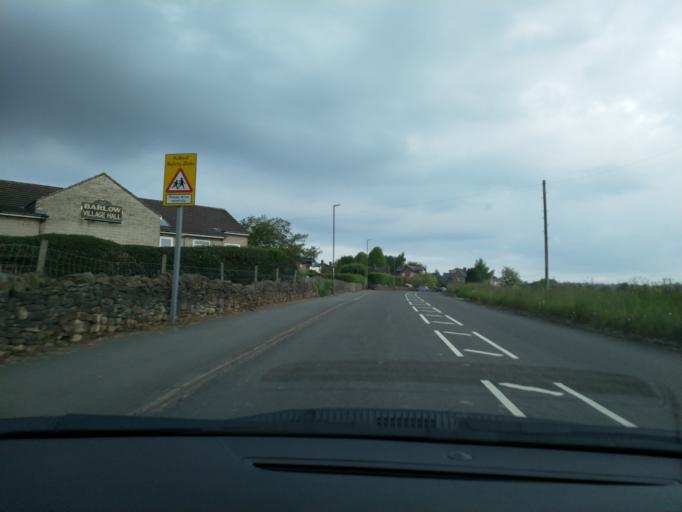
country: GB
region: England
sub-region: Derbyshire
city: Dronfield
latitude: 53.2708
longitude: -1.4868
